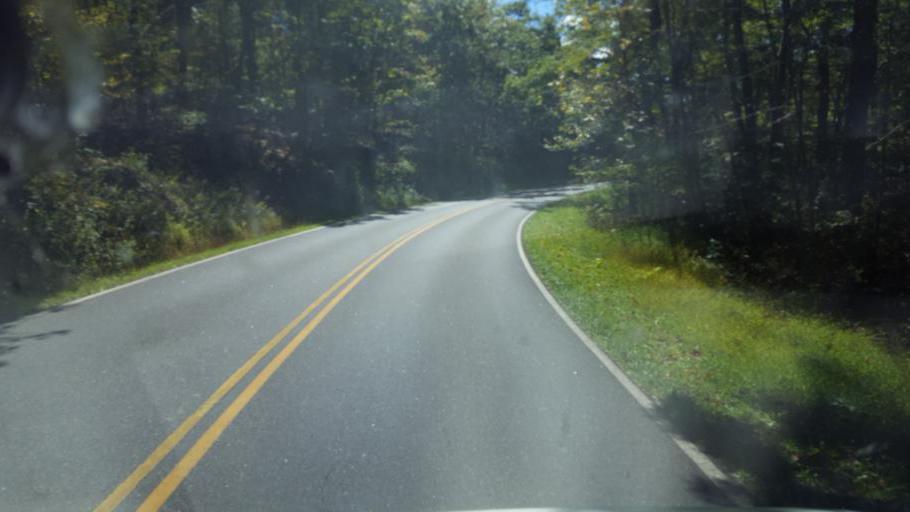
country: US
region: Virginia
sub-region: Page County
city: Stanley
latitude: 38.4371
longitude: -78.4798
